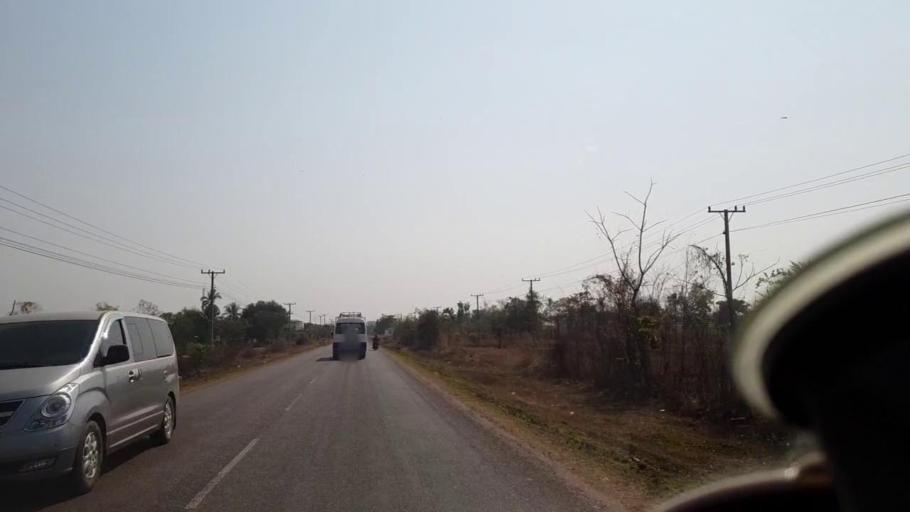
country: TH
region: Nong Khai
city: Nong Khai
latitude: 18.0552
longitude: 102.8316
